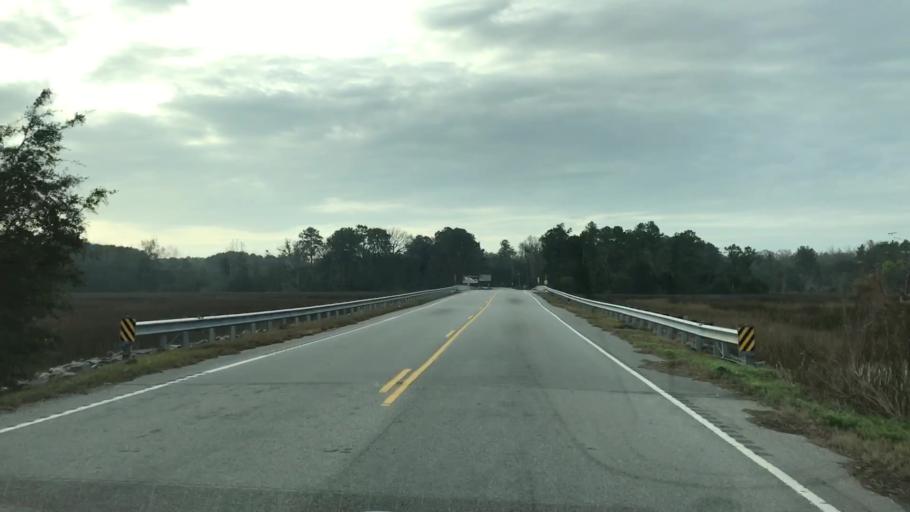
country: US
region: South Carolina
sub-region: Jasper County
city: Ridgeland
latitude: 32.5446
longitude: -80.9125
